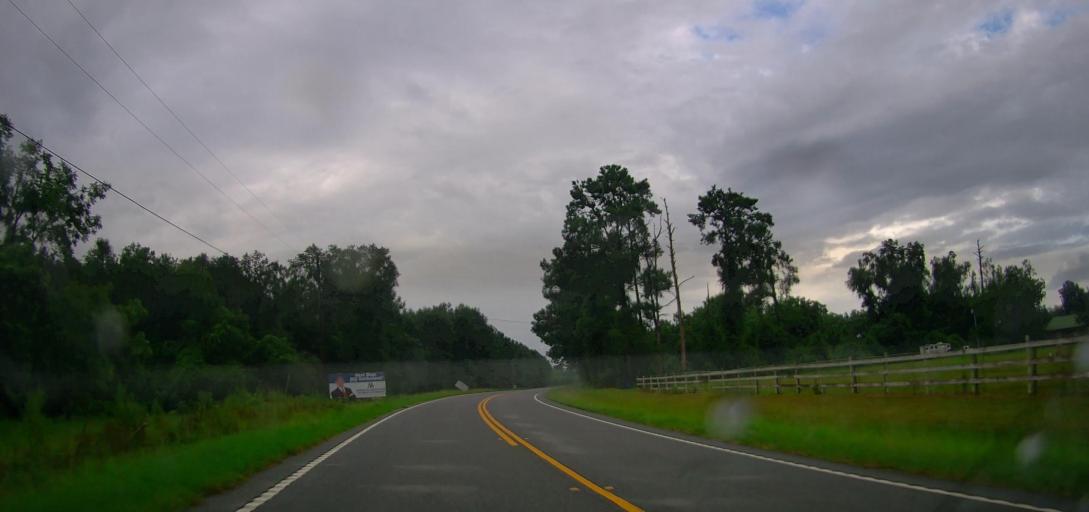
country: US
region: Georgia
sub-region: Ware County
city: Deenwood
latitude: 31.2696
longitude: -82.4028
